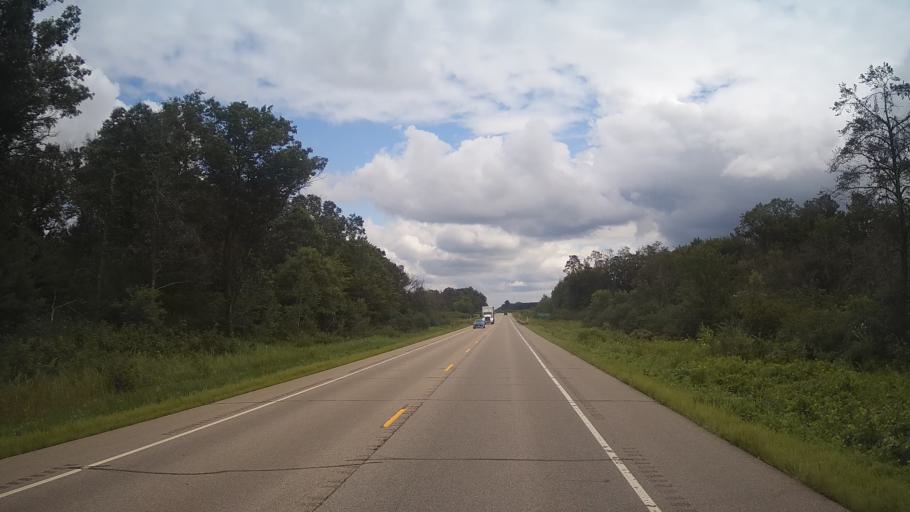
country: US
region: Wisconsin
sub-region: Adams County
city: Friendship
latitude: 44.0250
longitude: -89.7663
